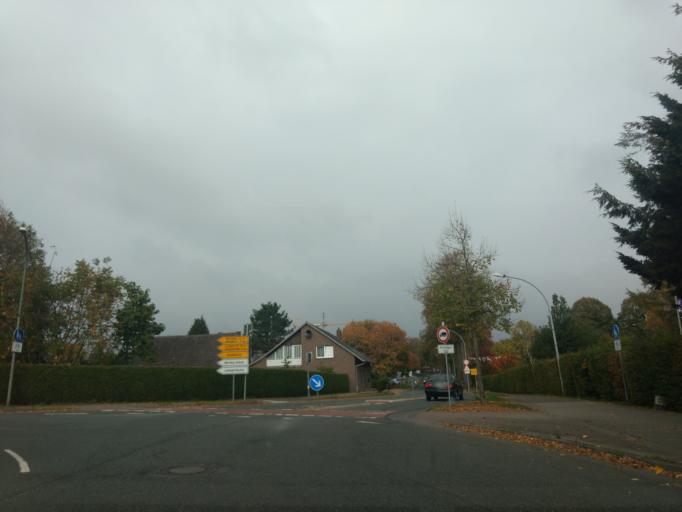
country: DE
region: Lower Saxony
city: Bad Iburg
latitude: 52.1492
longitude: 8.0490
